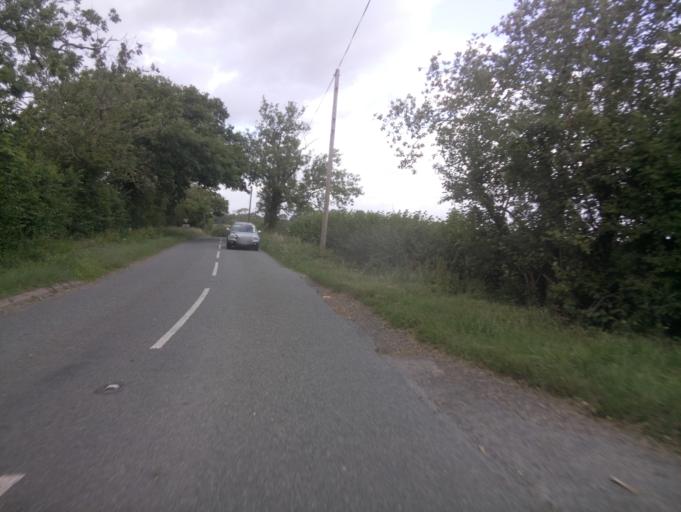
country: GB
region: England
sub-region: Gloucestershire
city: Moreton in Marsh
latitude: 52.0481
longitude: -1.7099
